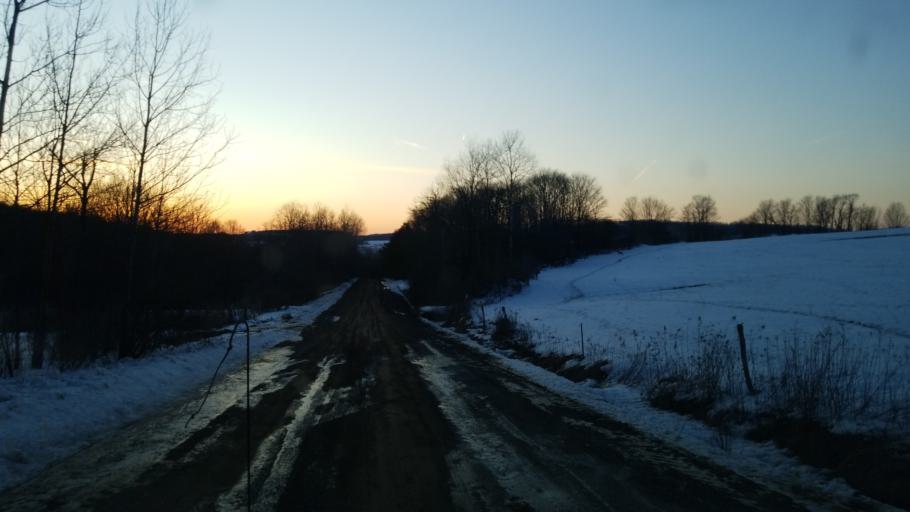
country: US
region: New York
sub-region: Allegany County
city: Andover
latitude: 42.0082
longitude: -77.7502
